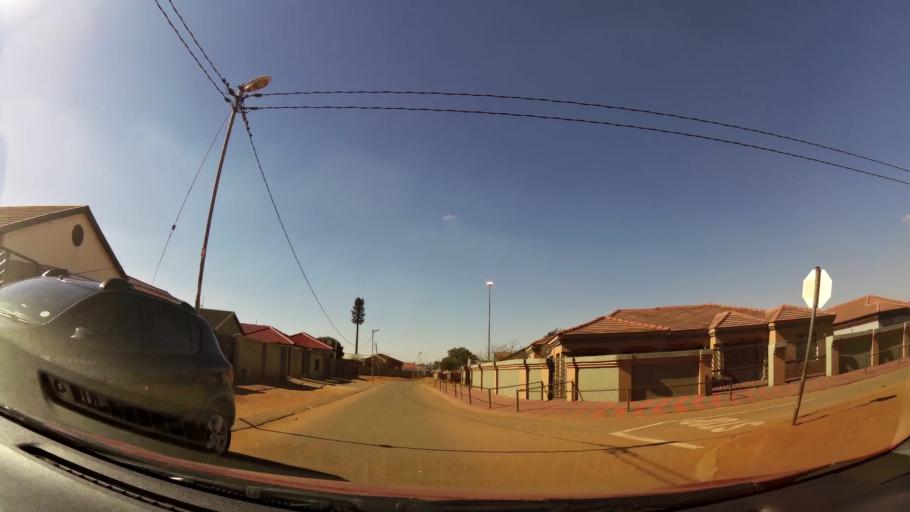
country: ZA
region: Gauteng
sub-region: City of Johannesburg Metropolitan Municipality
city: Soweto
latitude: -26.2427
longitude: 27.8061
